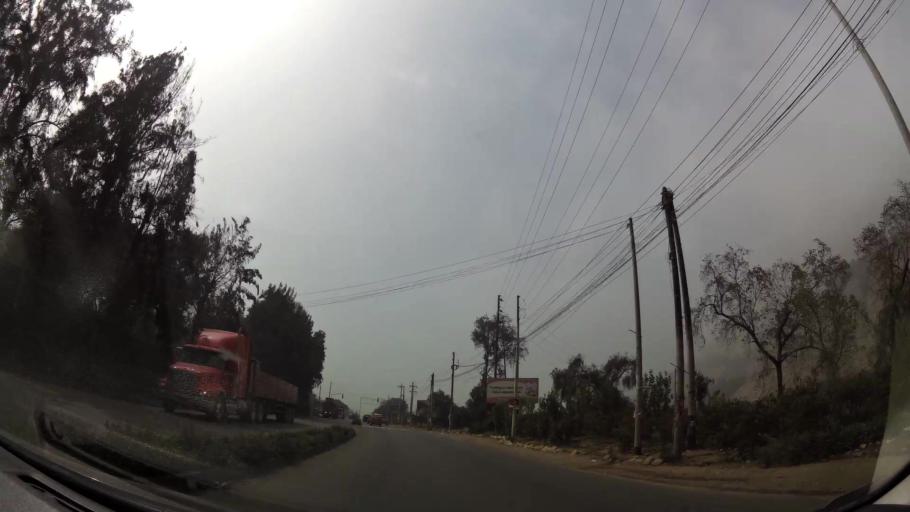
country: PE
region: Lima
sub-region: Lima
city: Chosica
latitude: -11.9620
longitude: -76.7383
